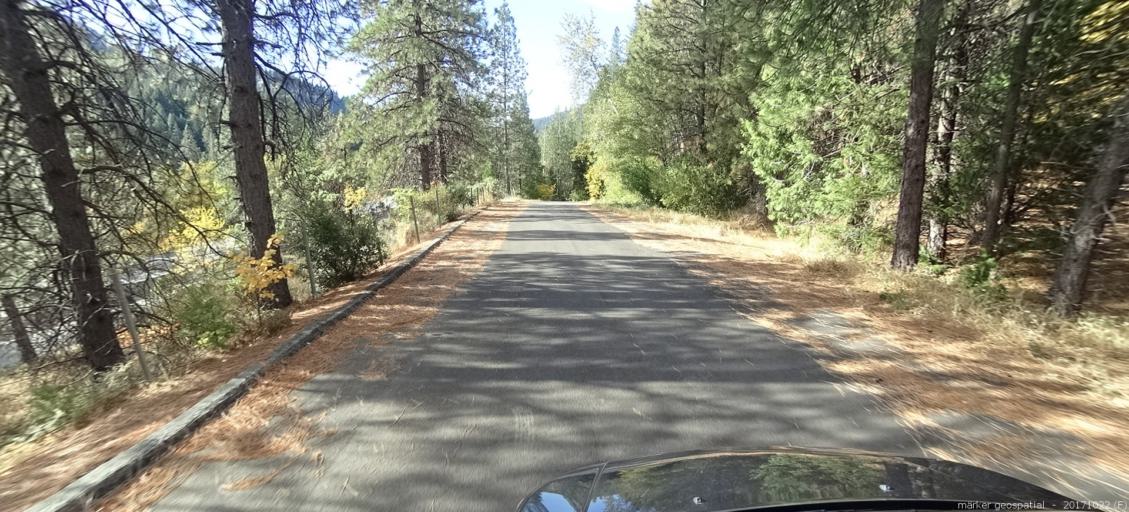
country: US
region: California
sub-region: Siskiyou County
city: Dunsmuir
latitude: 41.1041
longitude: -122.3381
